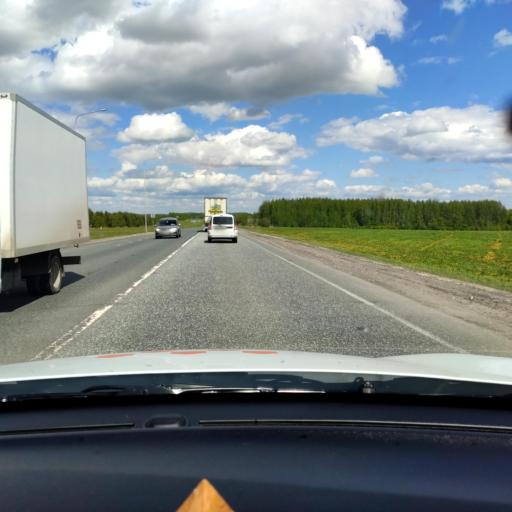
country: RU
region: Tatarstan
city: Verkhniy Uslon
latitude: 55.6618
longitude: 48.8592
